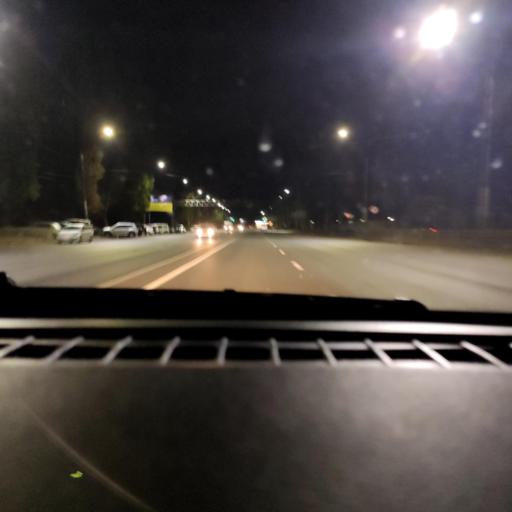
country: RU
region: Voronezj
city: Voronezh
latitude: 51.7044
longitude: 39.2758
